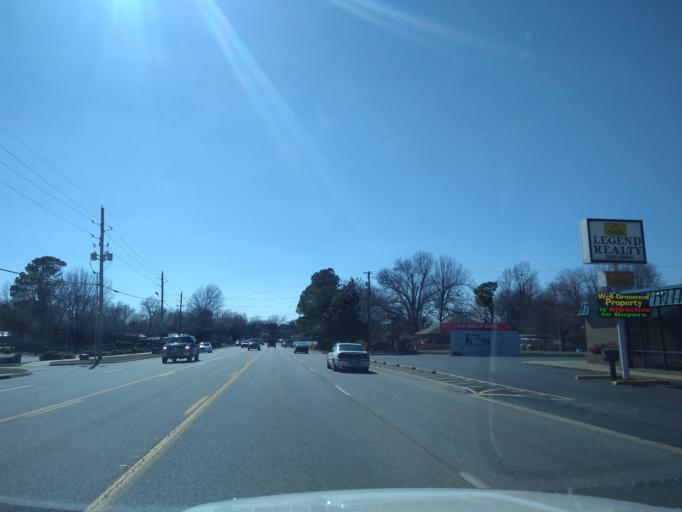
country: US
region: Arkansas
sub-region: Washington County
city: Farmington
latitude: 36.0442
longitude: -94.2318
